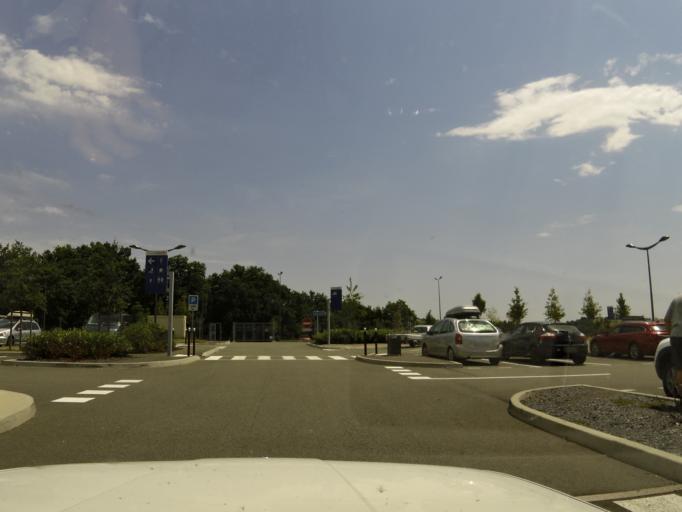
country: FR
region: Rhone-Alpes
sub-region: Departement de la Loire
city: Bussieres
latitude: 45.8507
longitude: 4.2256
